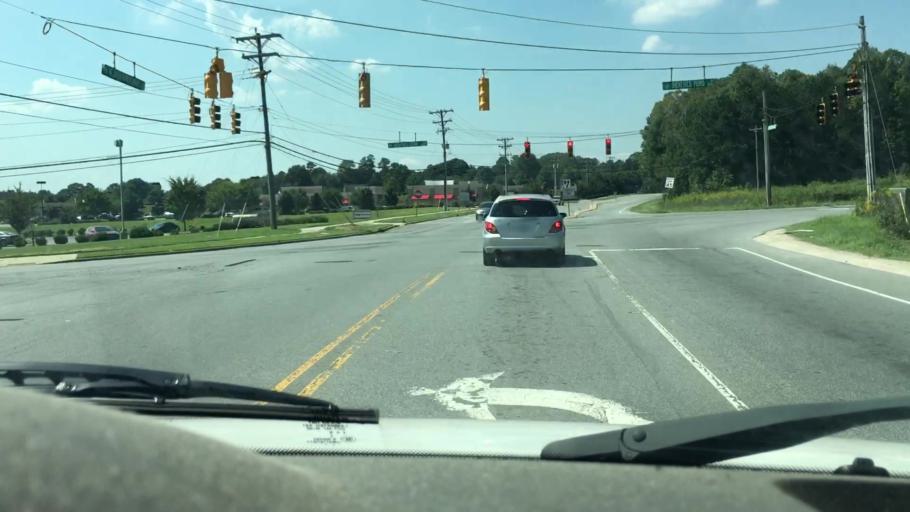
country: US
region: North Carolina
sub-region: Mecklenburg County
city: Huntersville
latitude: 35.3467
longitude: -80.8850
